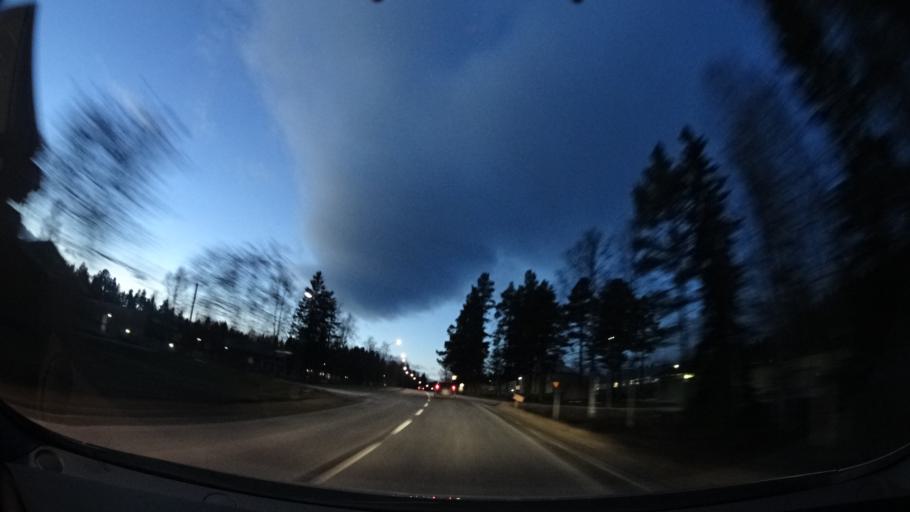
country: SE
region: Vaesterbotten
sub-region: Dorotea Kommun
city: Dorotea
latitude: 64.2581
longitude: 16.4277
